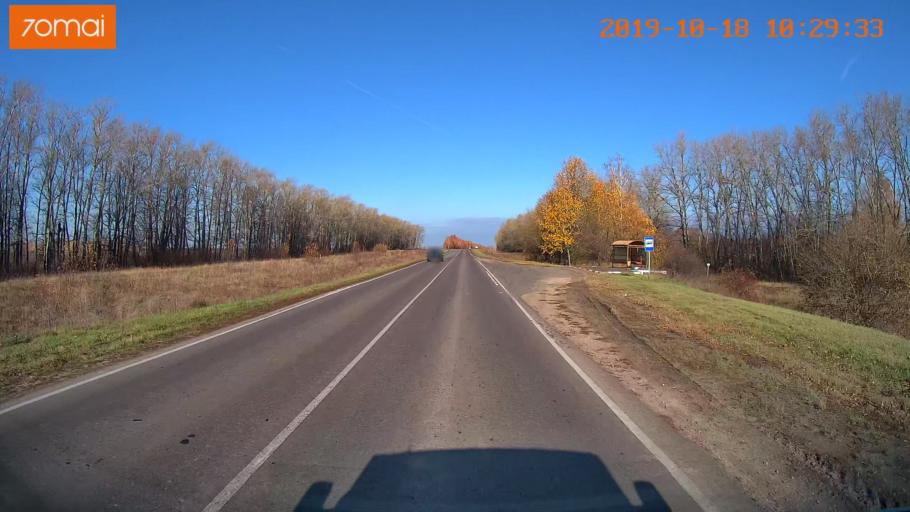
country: RU
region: Tula
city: Kurkino
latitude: 53.4528
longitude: 38.6550
